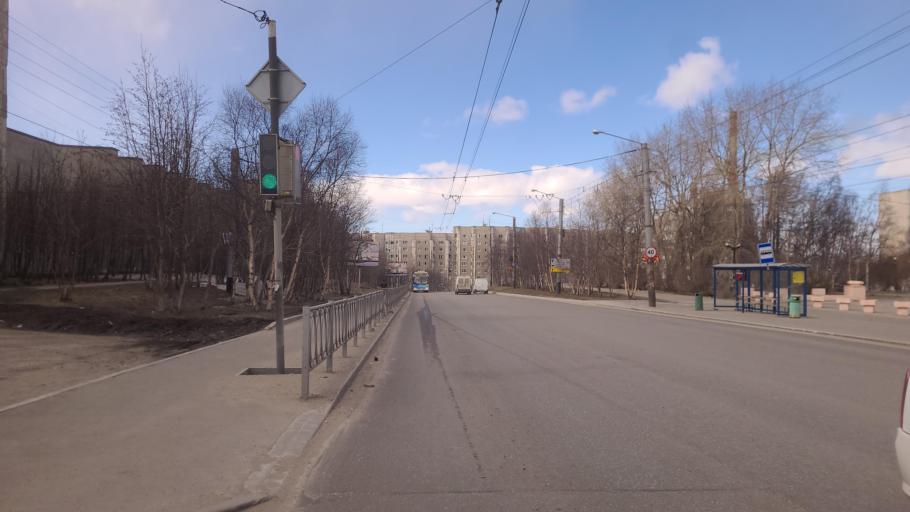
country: RU
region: Murmansk
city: Murmansk
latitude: 68.9537
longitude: 33.0669
